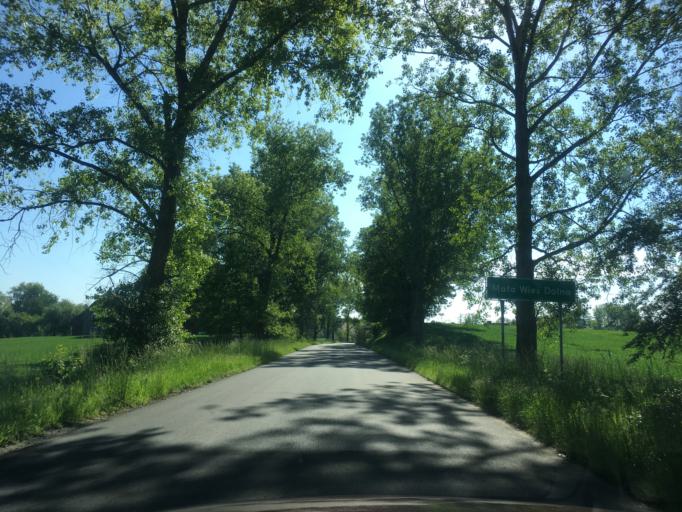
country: PL
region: Lower Silesian Voivodeship
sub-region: Powiat zgorzelecki
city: Sulikow
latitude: 51.0936
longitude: 15.0433
